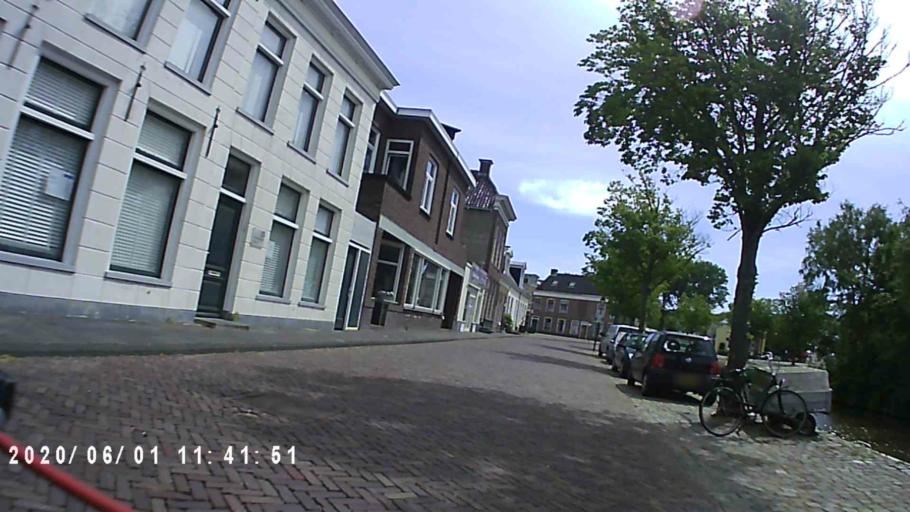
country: NL
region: Friesland
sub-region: Gemeente Harlingen
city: Harlingen
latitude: 53.1717
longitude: 5.4210
